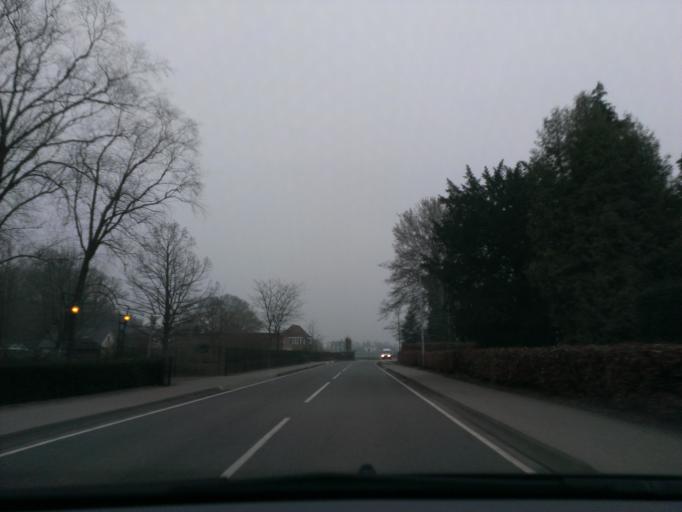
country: NL
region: Gelderland
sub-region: Gemeente Voorst
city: Twello
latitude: 52.2481
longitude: 6.1162
